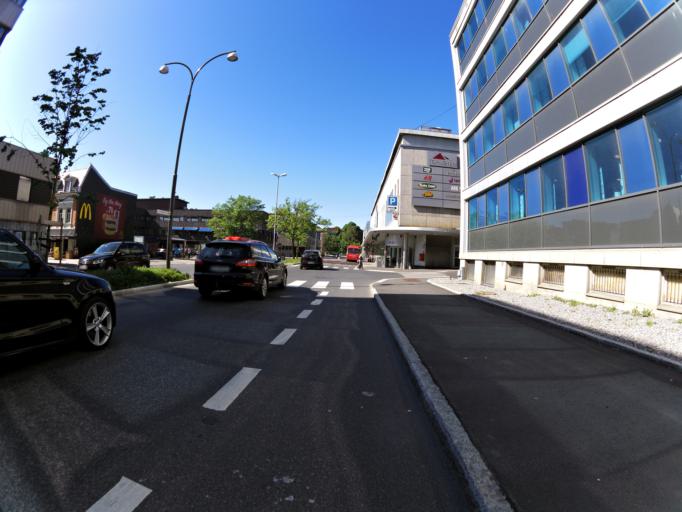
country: NO
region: Ostfold
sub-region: Fredrikstad
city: Fredrikstad
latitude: 59.2132
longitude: 10.9392
